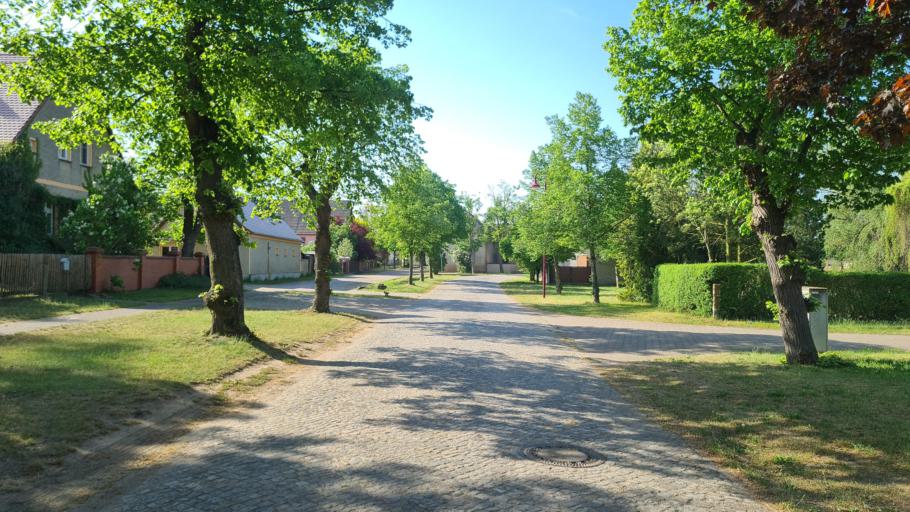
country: DE
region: Saxony
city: Arzberg
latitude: 51.5860
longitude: 13.1752
